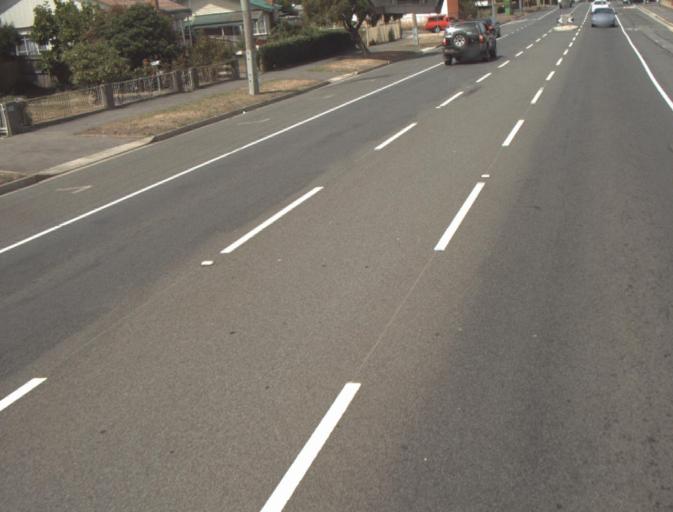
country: AU
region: Tasmania
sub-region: Launceston
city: Mayfield
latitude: -41.3876
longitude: 147.1272
